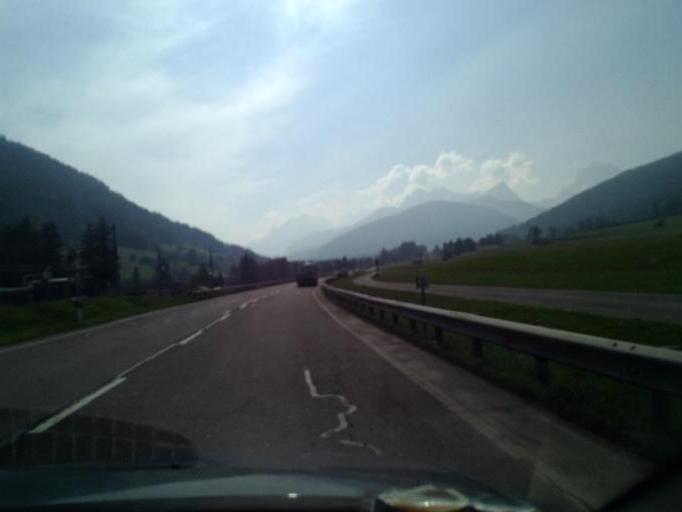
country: IT
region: Trentino-Alto Adige
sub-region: Bolzano
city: Monguelfo
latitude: 46.7512
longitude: 12.1120
